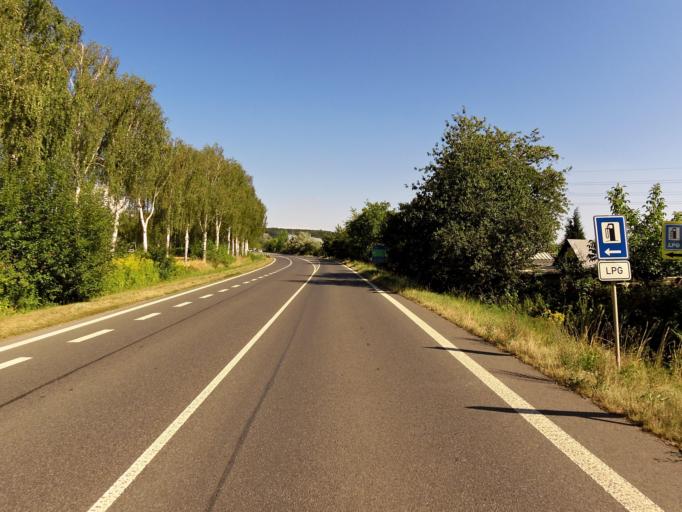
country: CZ
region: Central Bohemia
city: Mnichovo Hradiste
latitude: 50.5156
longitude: 14.9662
